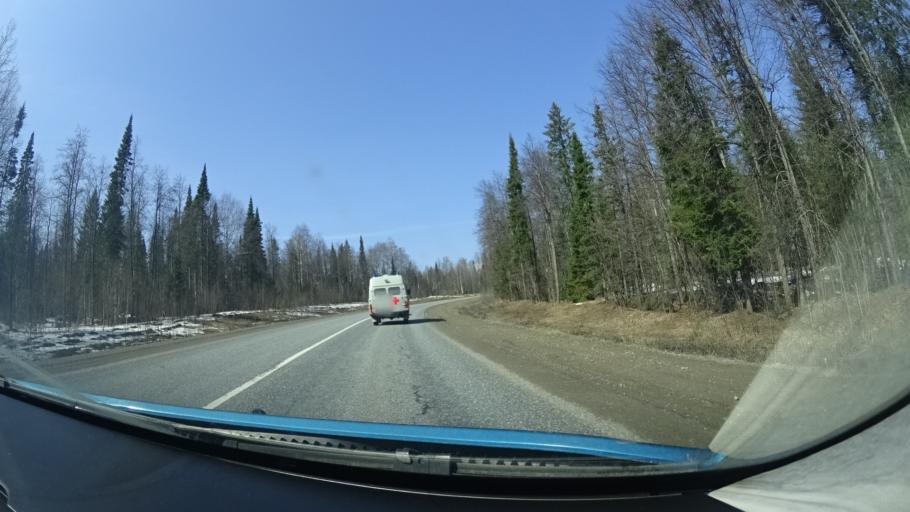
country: RU
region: Perm
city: Yugo-Kamskiy
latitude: 57.5975
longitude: 55.6550
